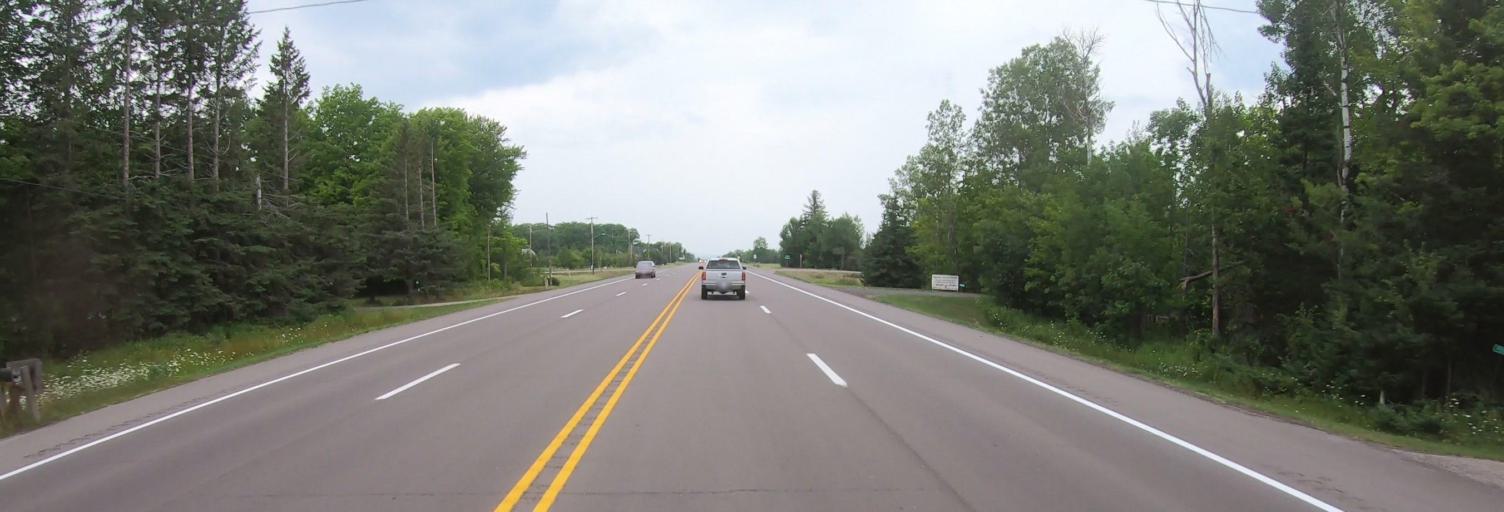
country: US
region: Michigan
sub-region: Houghton County
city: Dollar Bay
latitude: 46.9809
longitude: -88.4686
